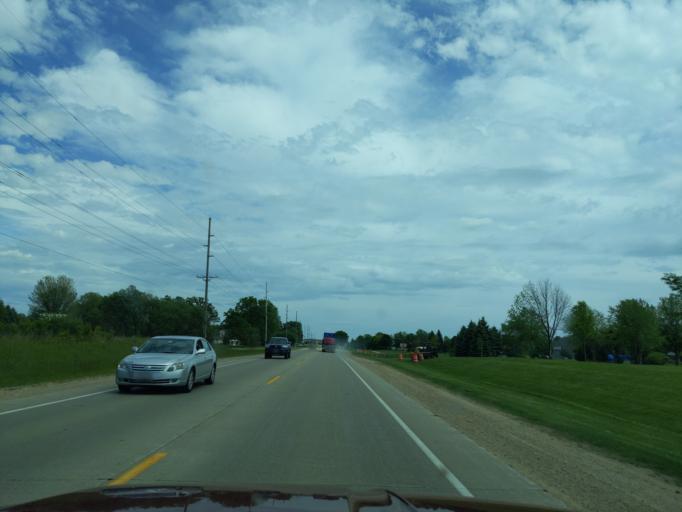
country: US
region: Wisconsin
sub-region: Dane County
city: Sun Prairie
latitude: 43.1906
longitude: -89.2800
